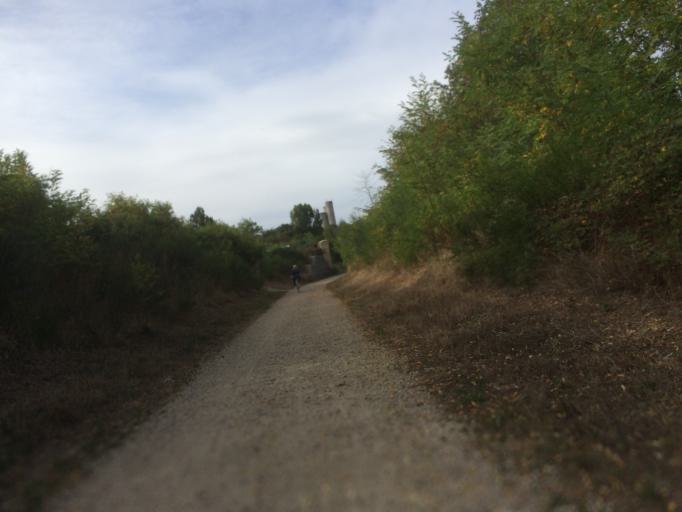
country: FR
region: Ile-de-France
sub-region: Departement de l'Essonne
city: Limours
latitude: 48.6467
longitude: 2.0657
